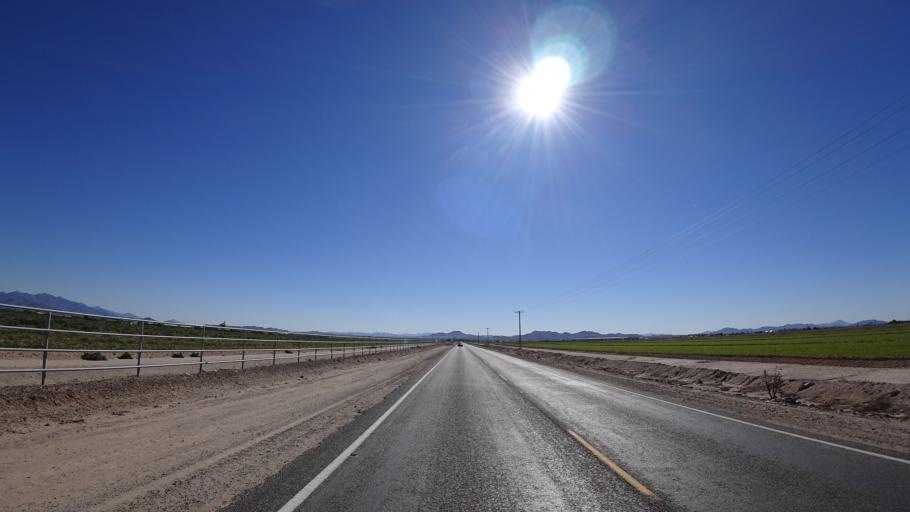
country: US
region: Arizona
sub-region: Maricopa County
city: Buckeye
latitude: 33.4049
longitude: -112.5215
